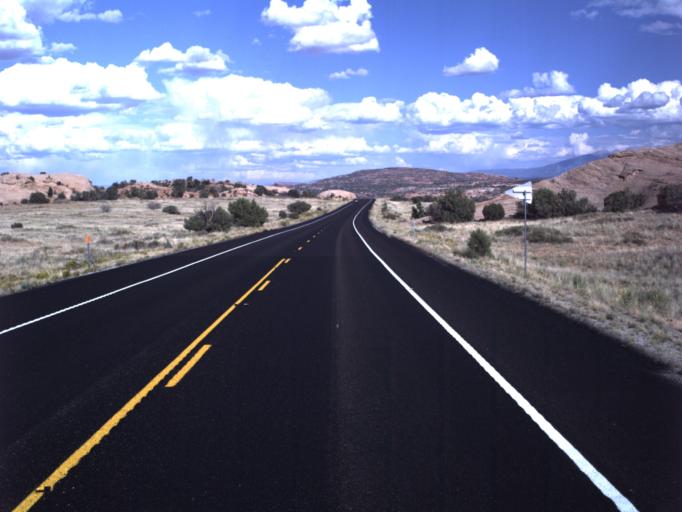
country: US
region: Utah
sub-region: Grand County
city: Moab
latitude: 38.6368
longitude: -109.7604
